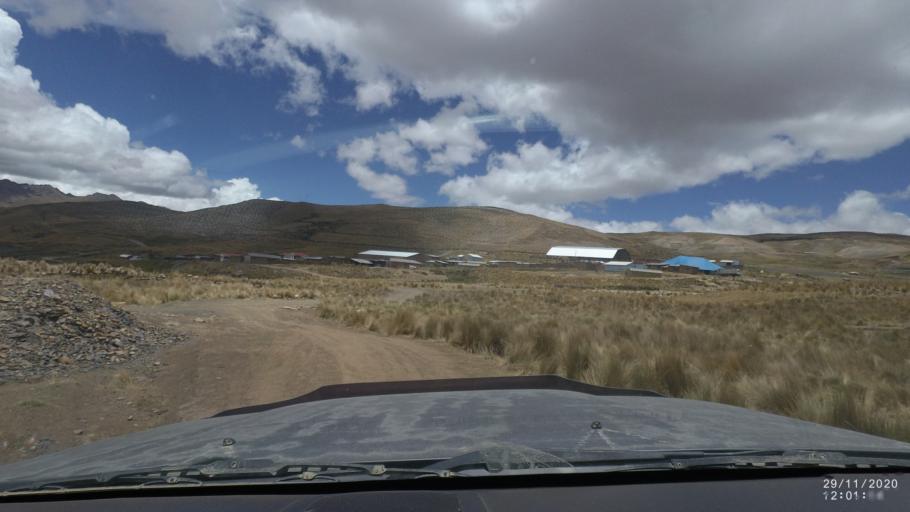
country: BO
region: Cochabamba
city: Cochabamba
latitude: -17.1514
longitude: -66.2810
